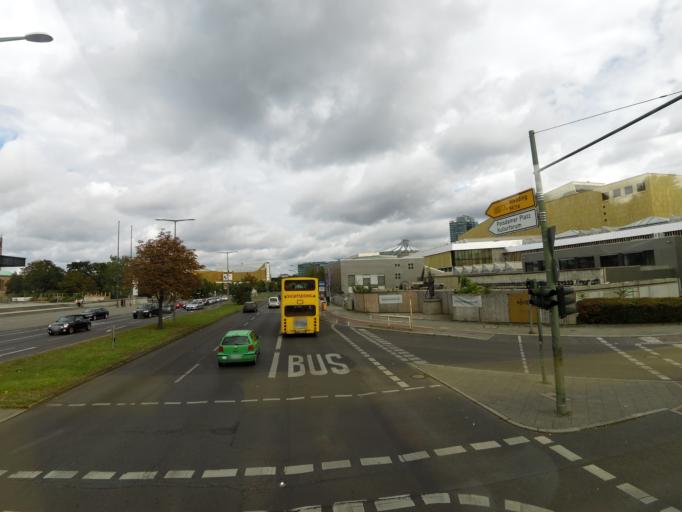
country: DE
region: Berlin
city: Tiergarten Bezirk
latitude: 52.5063
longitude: 13.3687
